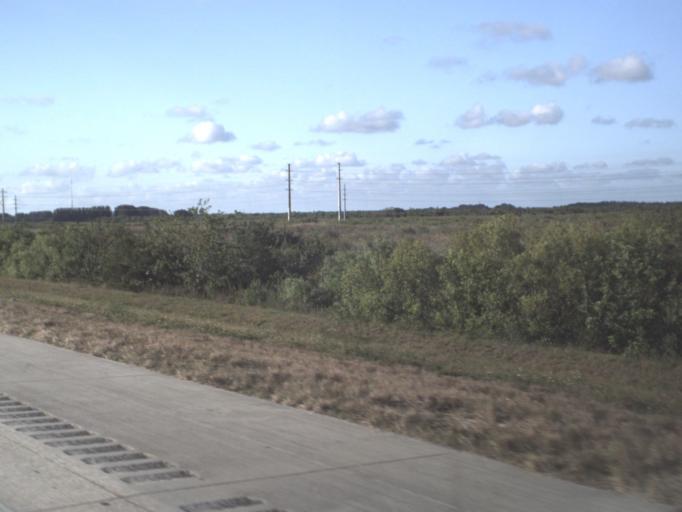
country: US
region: Florida
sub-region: Brevard County
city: Cocoa West
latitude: 28.3221
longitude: -80.7697
